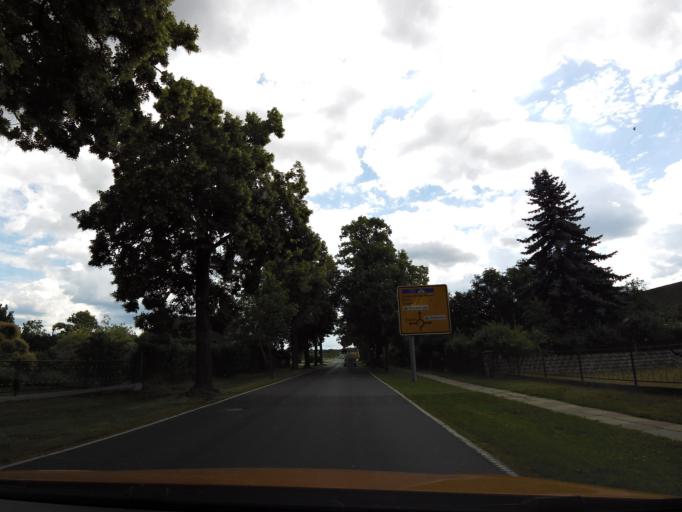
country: DE
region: Brandenburg
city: Rangsdorf
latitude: 52.3185
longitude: 13.4417
